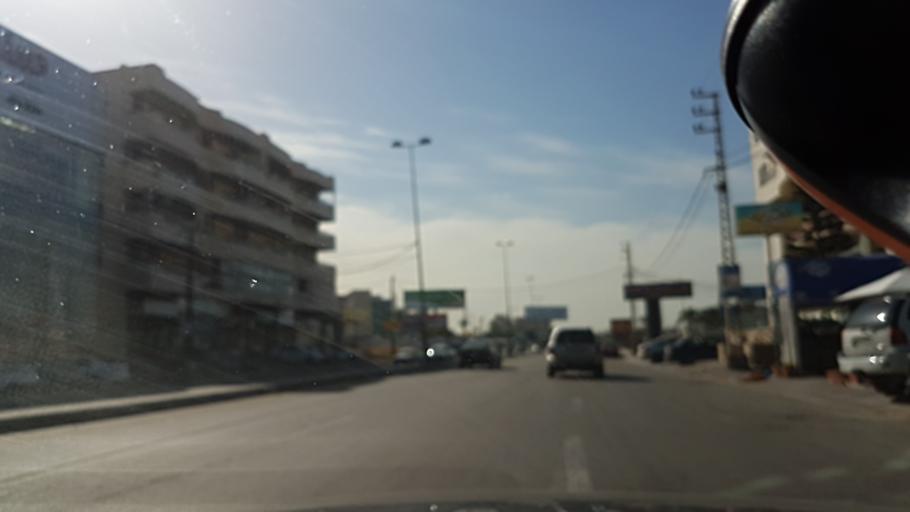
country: LB
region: Liban-Sud
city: Sidon
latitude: 33.5850
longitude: 35.3872
